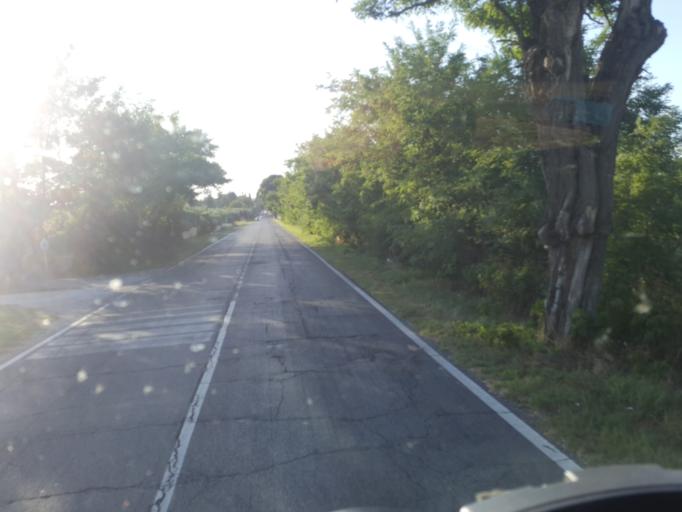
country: IT
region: Latium
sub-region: Citta metropolitana di Roma Capitale
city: Bivio di Capanelle
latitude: 42.1271
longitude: 12.5742
